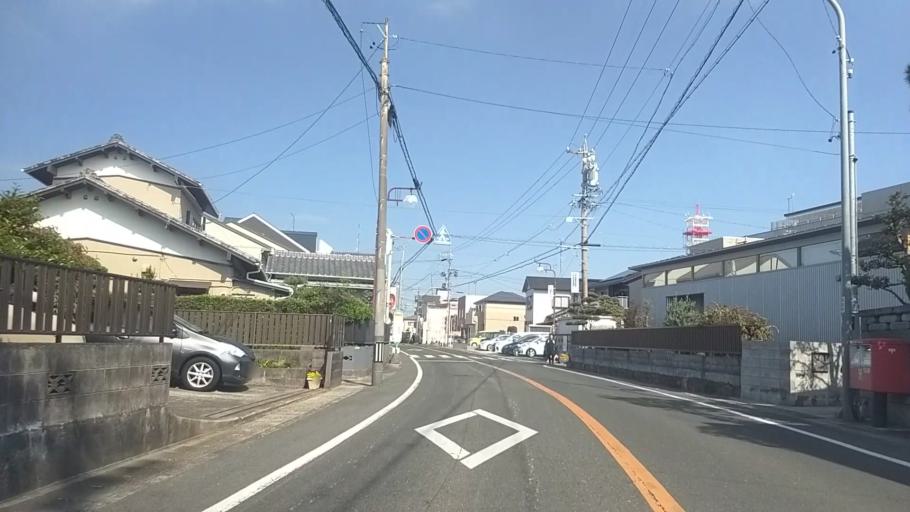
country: JP
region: Shizuoka
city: Hamamatsu
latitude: 34.7040
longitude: 137.7534
